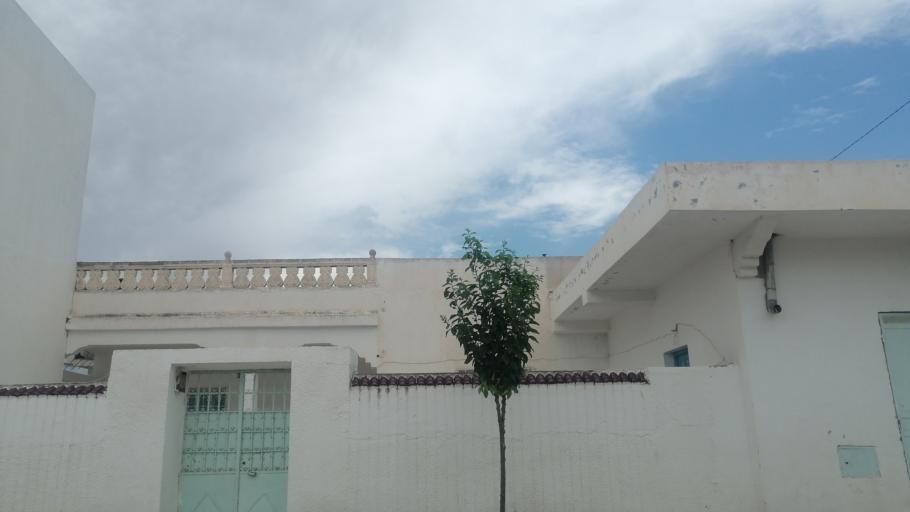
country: TN
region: Al Qayrawan
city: Sbikha
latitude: 36.1279
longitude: 10.0914
